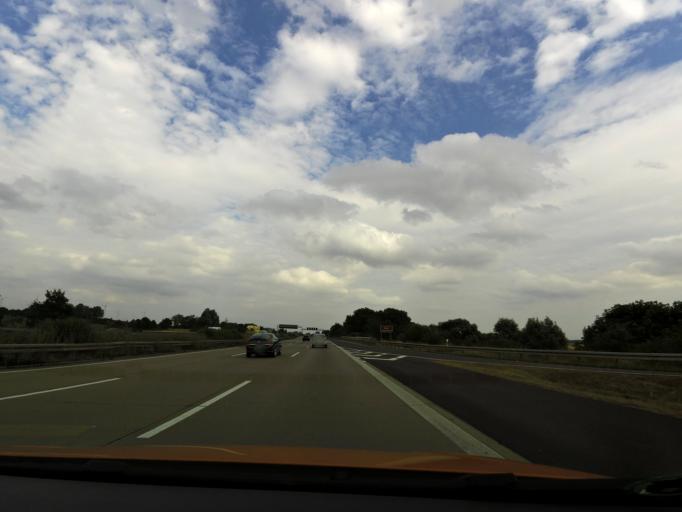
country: DE
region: Saxony-Anhalt
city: Wefensleben
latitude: 52.2071
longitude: 11.1374
